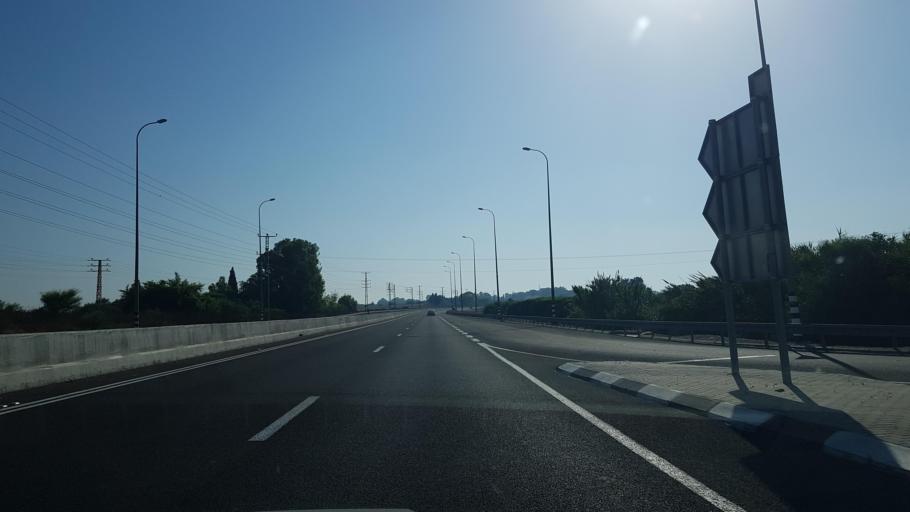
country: IL
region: Southern District
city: Ashqelon
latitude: 31.6859
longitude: 34.6604
